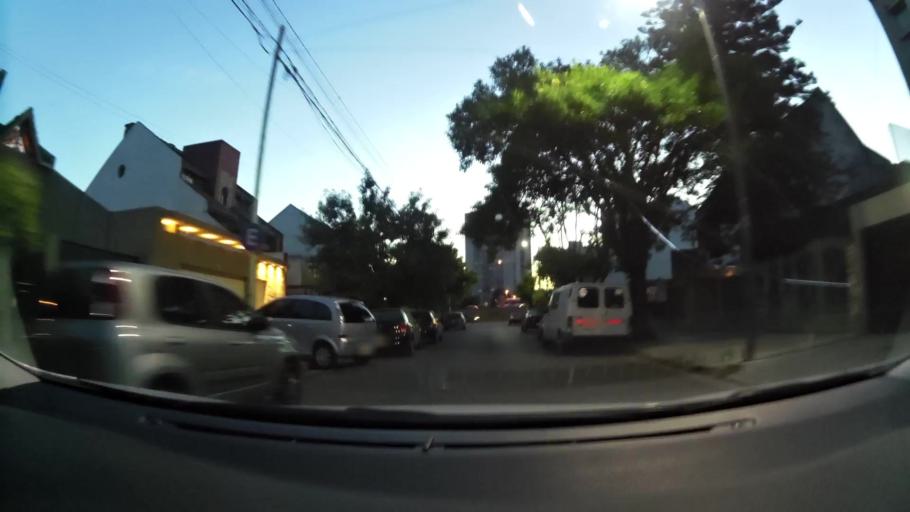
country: AR
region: Buenos Aires F.D.
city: Villa Lugano
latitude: -34.6915
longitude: -58.4775
